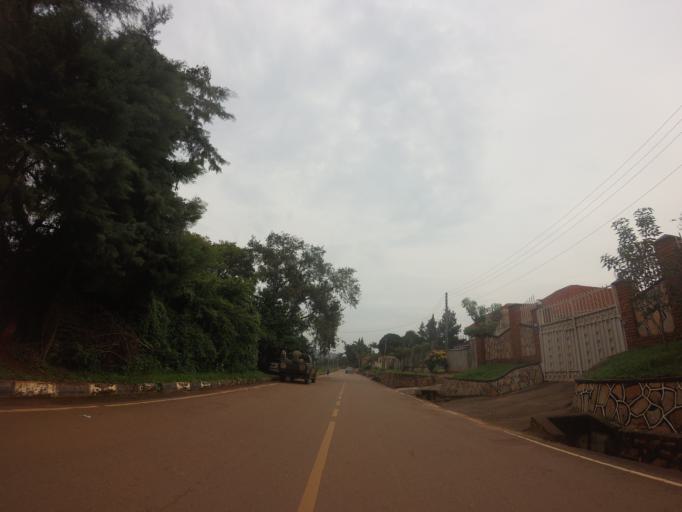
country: UG
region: Central Region
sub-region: Wakiso District
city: Kireka
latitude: 0.3491
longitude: 32.6220
